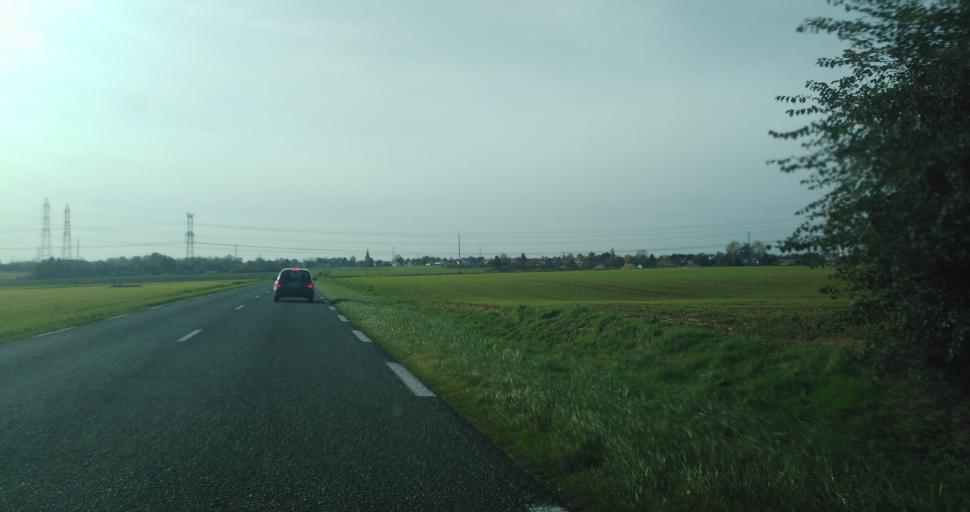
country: FR
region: Haute-Normandie
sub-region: Departement de l'Eure
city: Hauville
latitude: 49.3580
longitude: 0.7404
